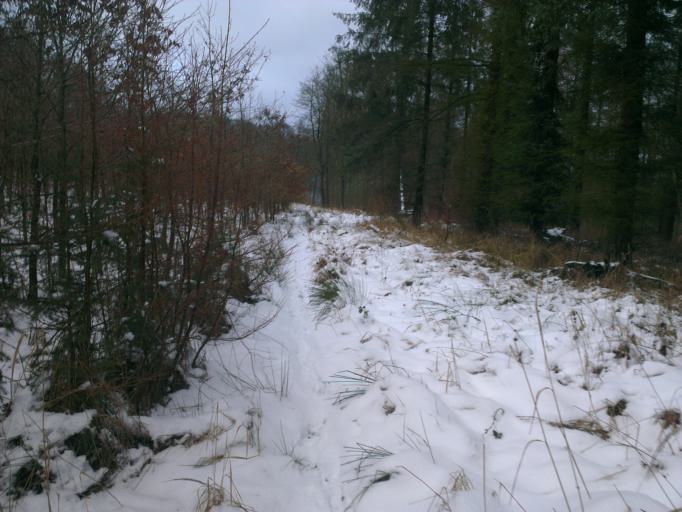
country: DK
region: Capital Region
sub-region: Frederikssund Kommune
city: Frederikssund
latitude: 55.8490
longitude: 12.0229
